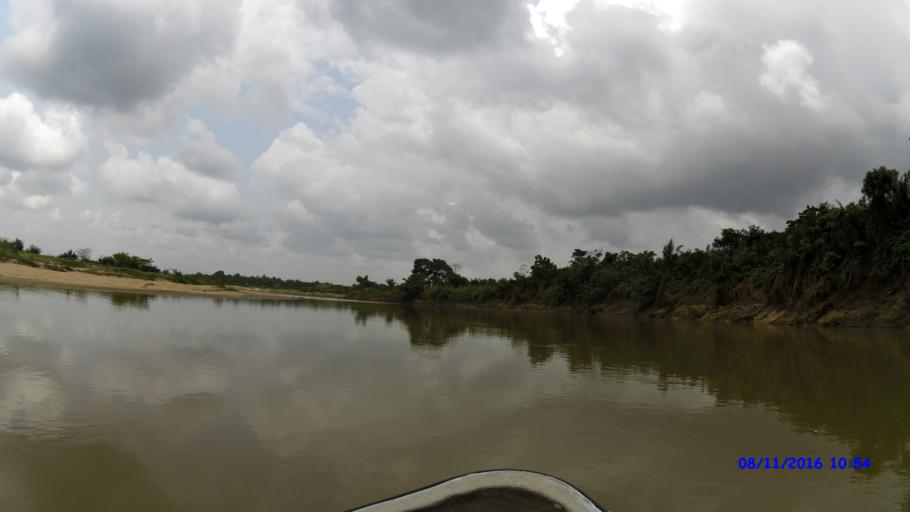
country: BJ
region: Mono
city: Lokossa
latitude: 6.4907
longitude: 1.7257
